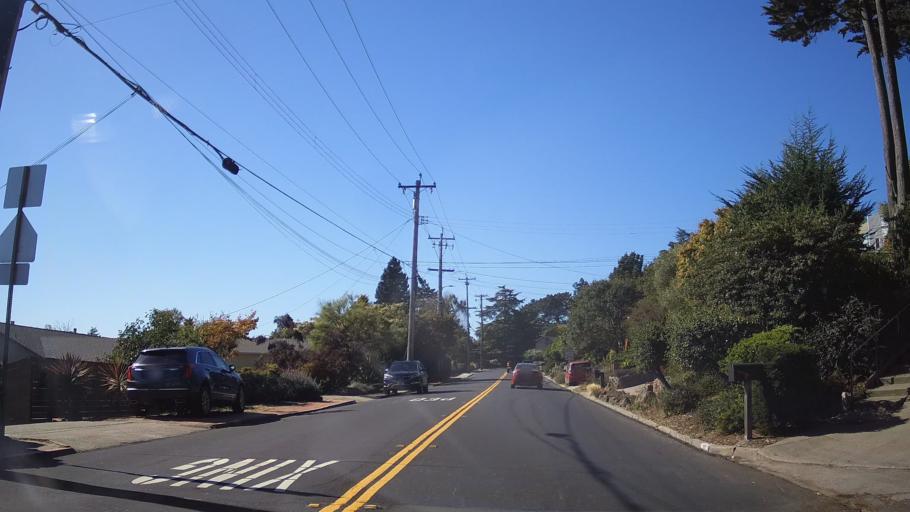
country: US
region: California
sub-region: Contra Costa County
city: Kensington
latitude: 37.9173
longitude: -122.2846
